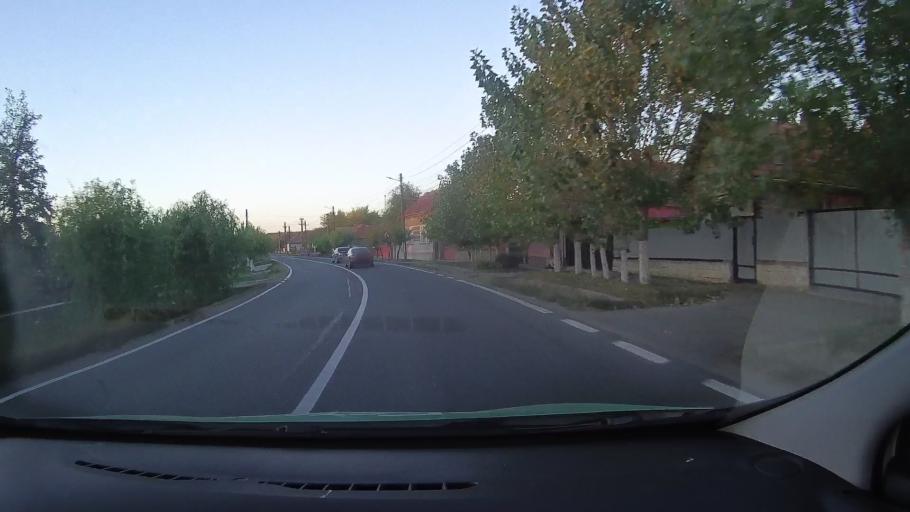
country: RO
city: Szekelyhid
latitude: 47.3578
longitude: 22.1118
